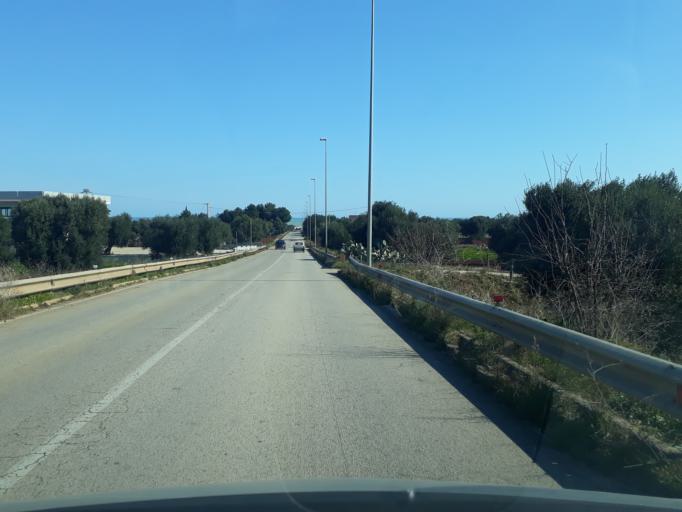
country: IT
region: Apulia
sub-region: Provincia di Brindisi
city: Fasano
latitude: 40.8990
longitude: 17.3388
